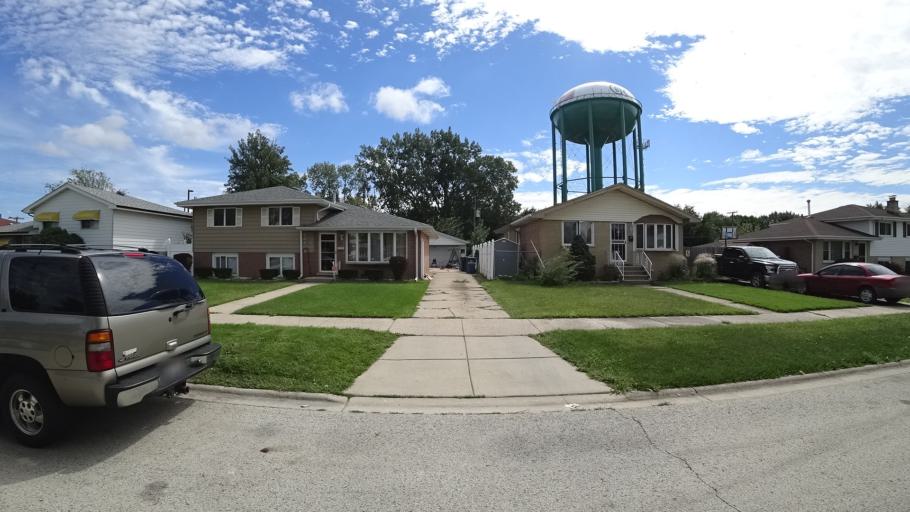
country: US
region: Illinois
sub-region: Cook County
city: Chicago Ridge
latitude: 41.7030
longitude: -87.7819
